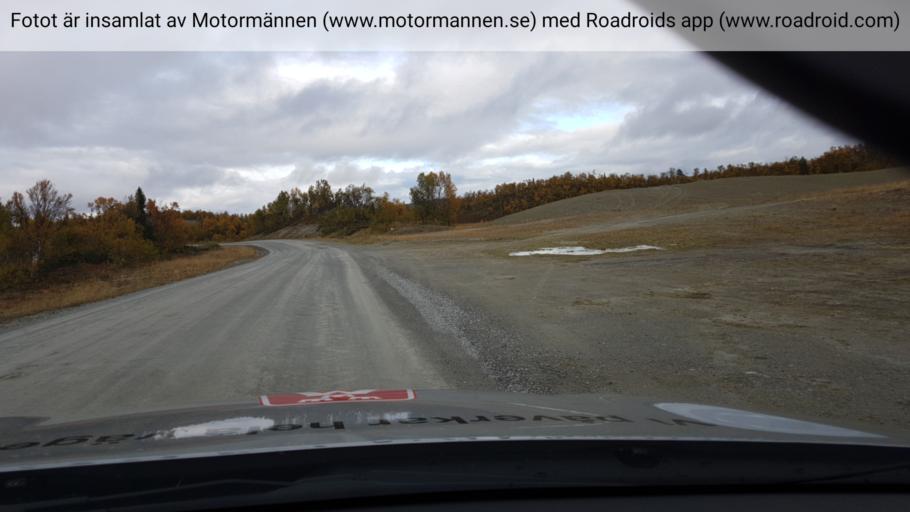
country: SE
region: Jaemtland
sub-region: Are Kommun
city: Are
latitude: 62.6359
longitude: 12.6518
